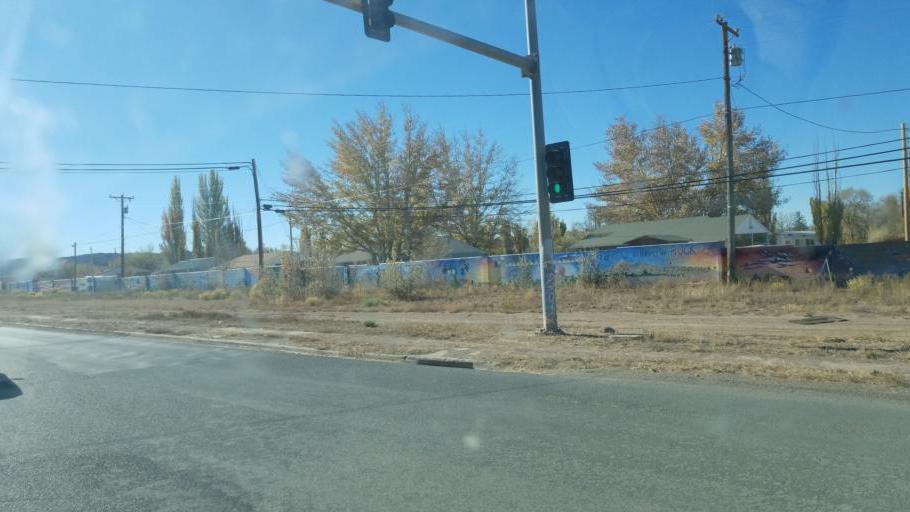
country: US
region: Arizona
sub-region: Apache County
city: Fort Defiance
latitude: 35.7342
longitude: -109.0594
